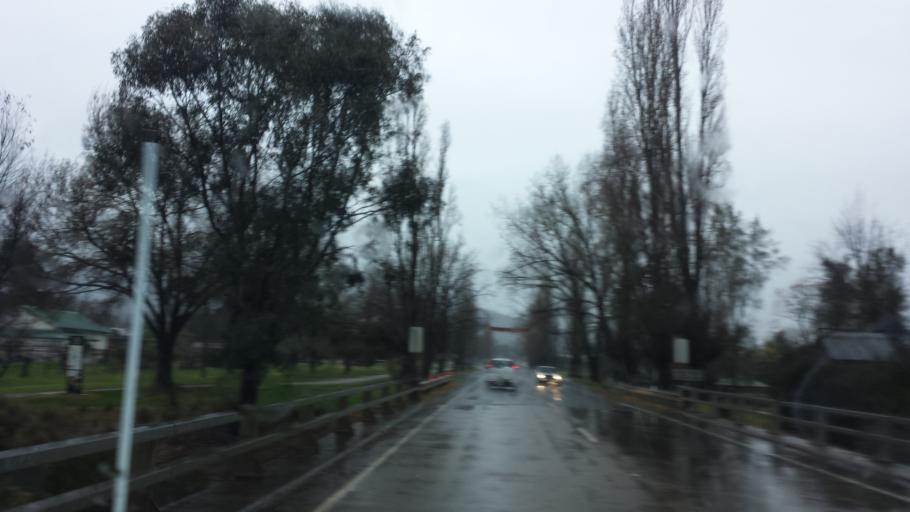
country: AU
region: Victoria
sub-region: Wangaratta
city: Wangaratta
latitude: -36.5535
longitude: 146.7119
